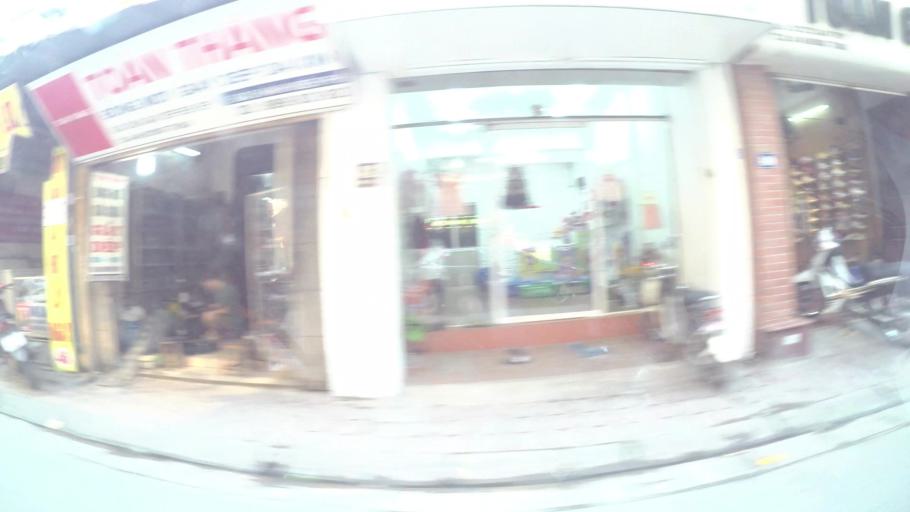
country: VN
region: Ha Noi
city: Thanh Xuan
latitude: 20.9989
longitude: 105.8188
